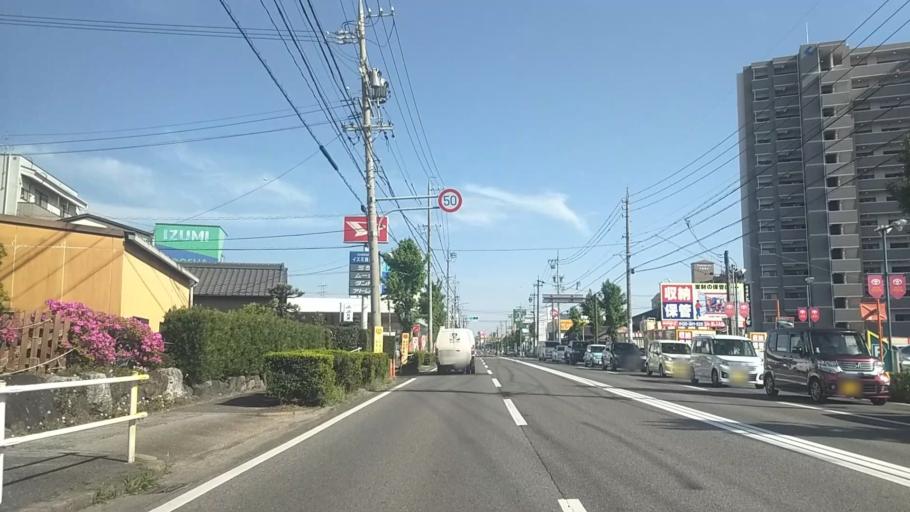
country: JP
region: Aichi
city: Anjo
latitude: 34.9626
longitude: 137.0693
